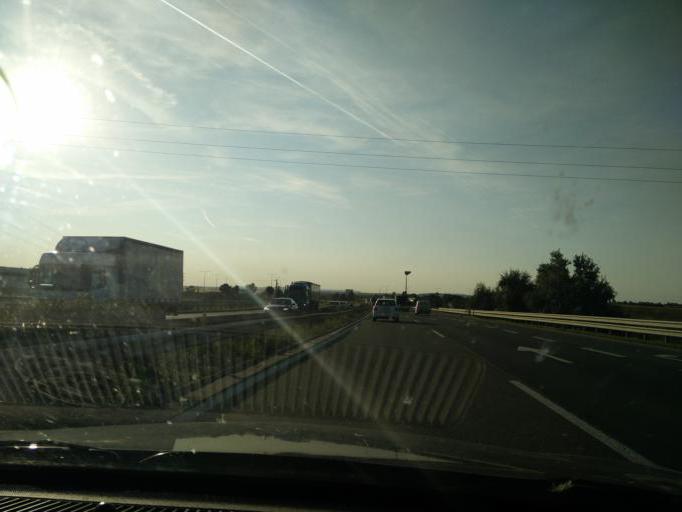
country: HU
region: Pest
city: Biatorbagy
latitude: 47.4930
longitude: 18.8233
